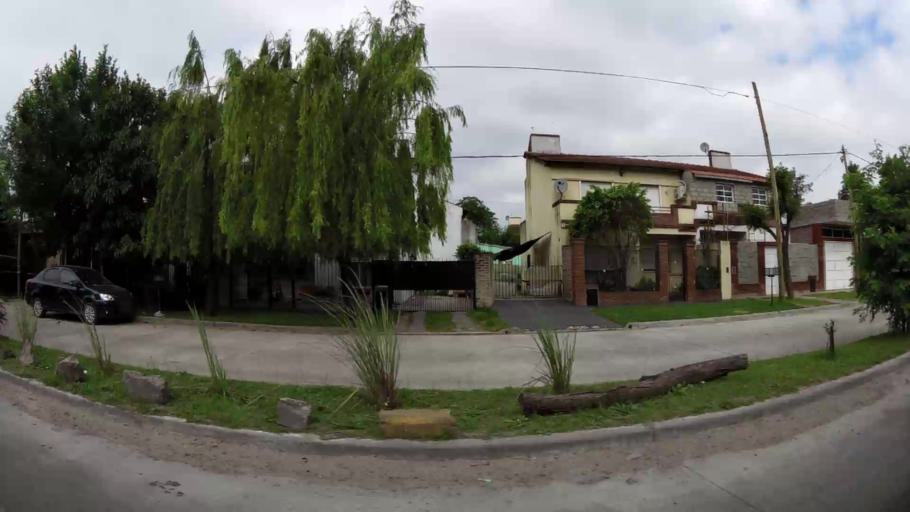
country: AR
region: Buenos Aires
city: San Justo
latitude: -34.7204
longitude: -58.5354
